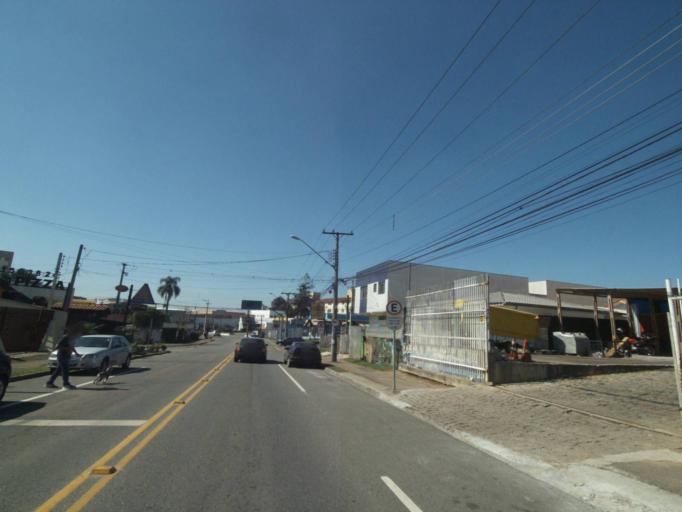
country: BR
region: Parana
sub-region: Curitiba
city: Curitiba
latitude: -25.3835
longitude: -49.2346
